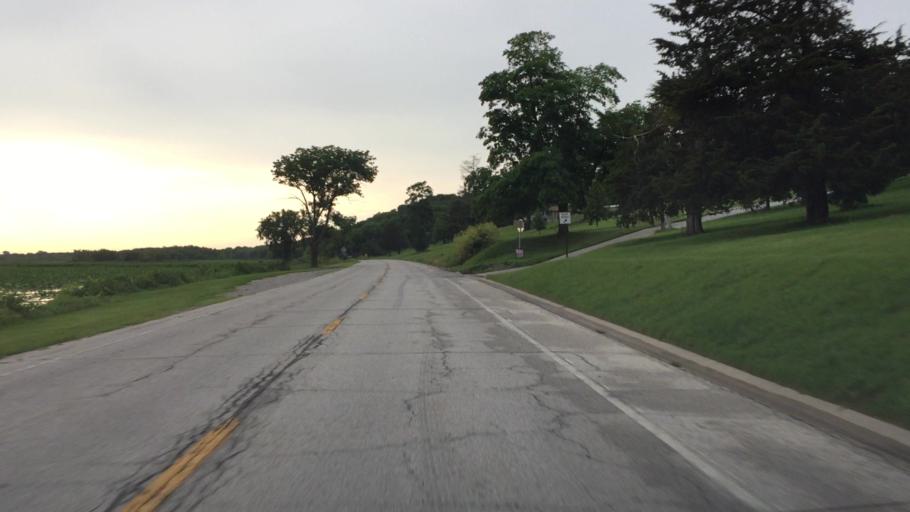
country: US
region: Illinois
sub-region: Hancock County
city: Nauvoo
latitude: 40.5262
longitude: -91.3687
